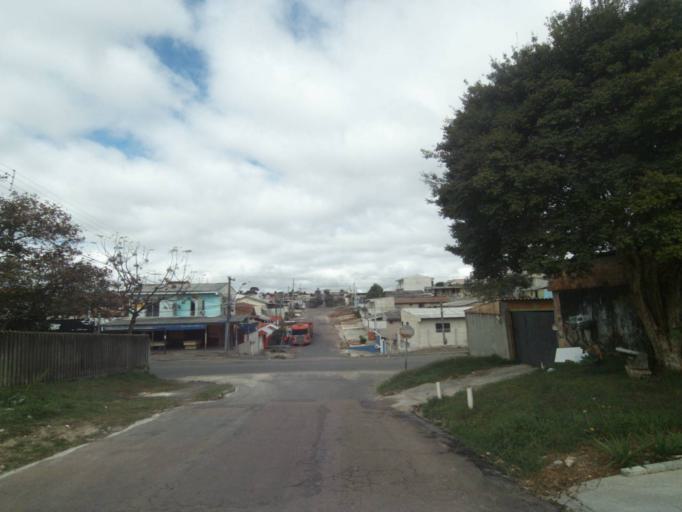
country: BR
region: Parana
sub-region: Sao Jose Dos Pinhais
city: Sao Jose dos Pinhais
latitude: -25.5401
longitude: -49.2895
